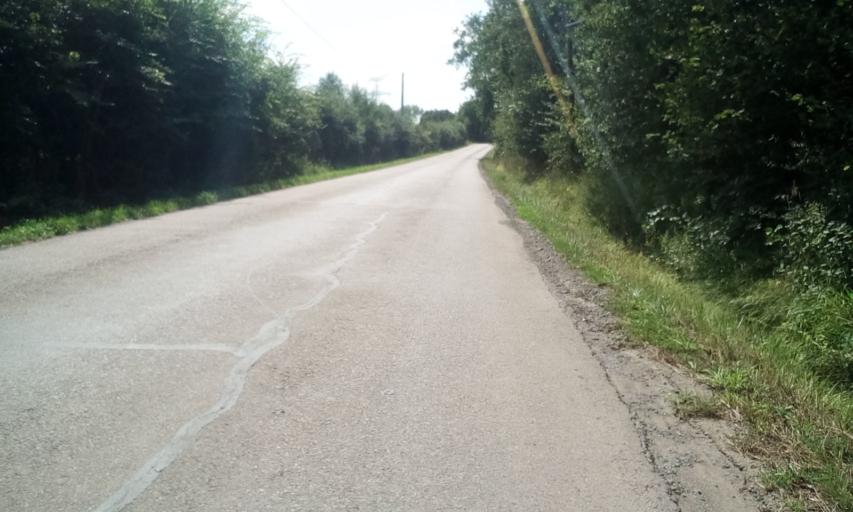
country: FR
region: Lower Normandy
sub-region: Departement du Calvados
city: Argences
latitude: 49.1393
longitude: -0.1554
